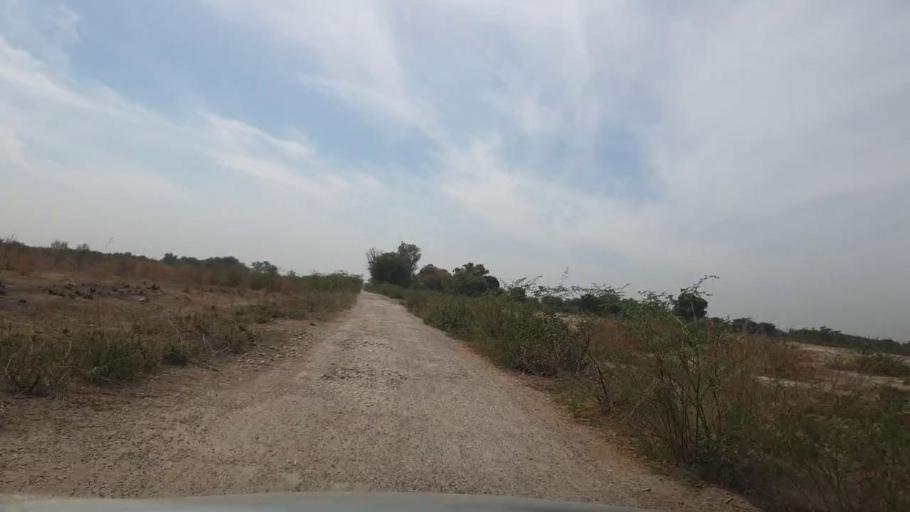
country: PK
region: Sindh
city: Nabisar
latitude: 25.1032
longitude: 69.6034
